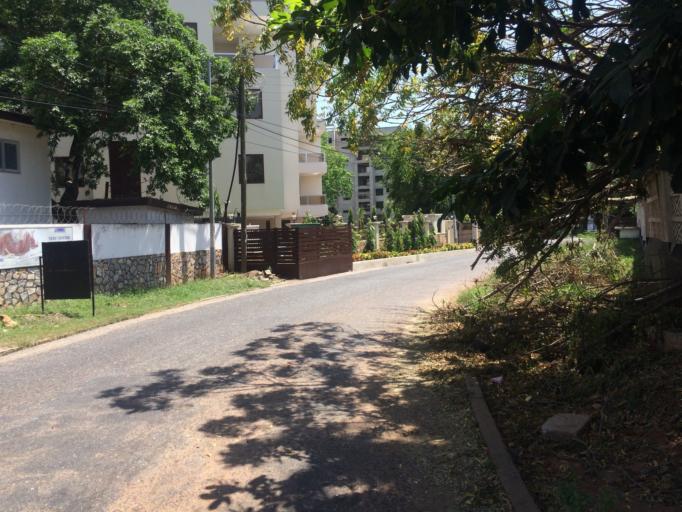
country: GH
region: Greater Accra
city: Accra
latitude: 5.5649
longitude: -0.1895
